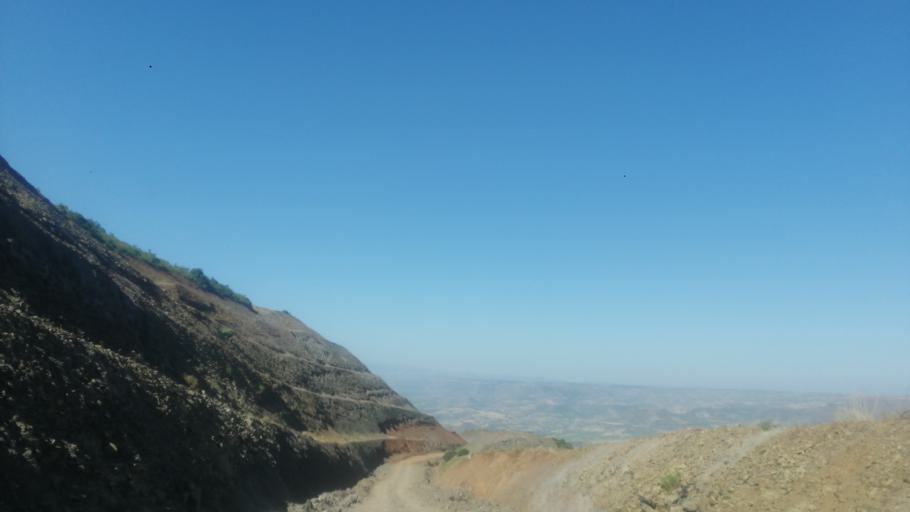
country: ET
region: Amhara
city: Addiet Canna
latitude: 11.1530
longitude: 37.8555
